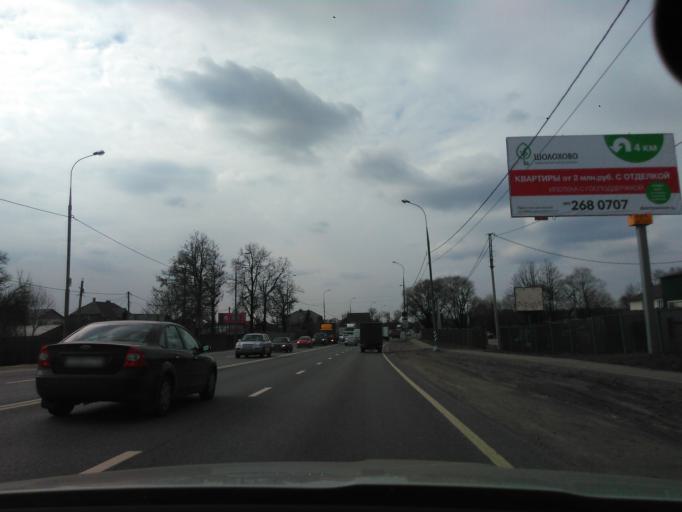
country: RU
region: Moskovskaya
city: Marfino
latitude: 56.0104
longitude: 37.5450
